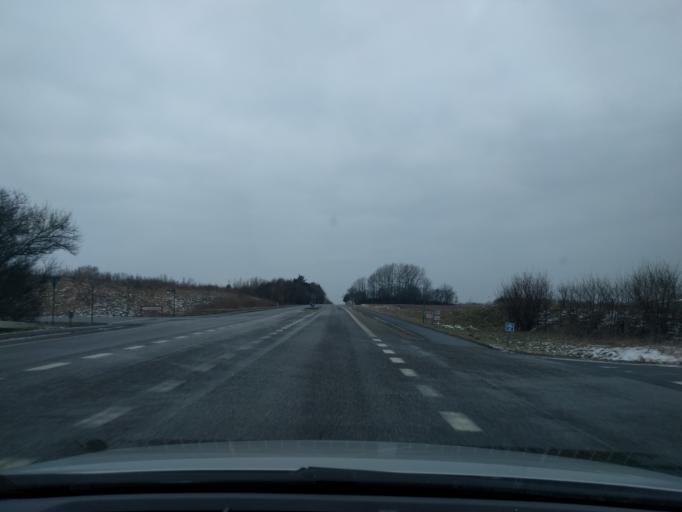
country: DK
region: South Denmark
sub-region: Middelfart Kommune
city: Strib
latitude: 55.4921
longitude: 9.7905
